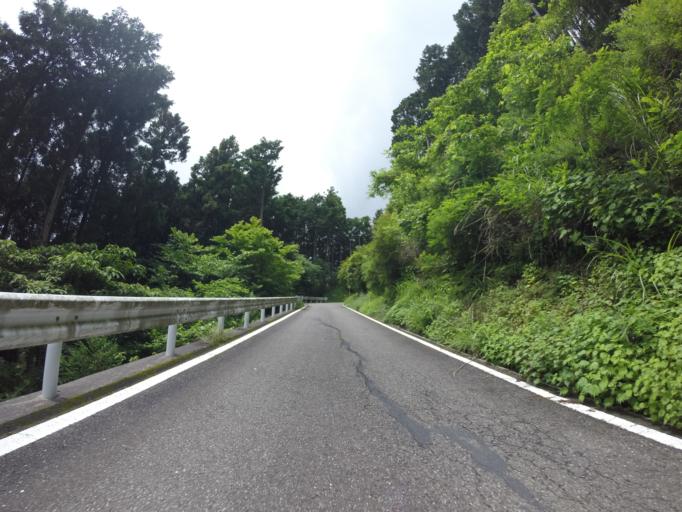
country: JP
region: Shizuoka
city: Shizuoka-shi
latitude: 35.0494
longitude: 138.3112
